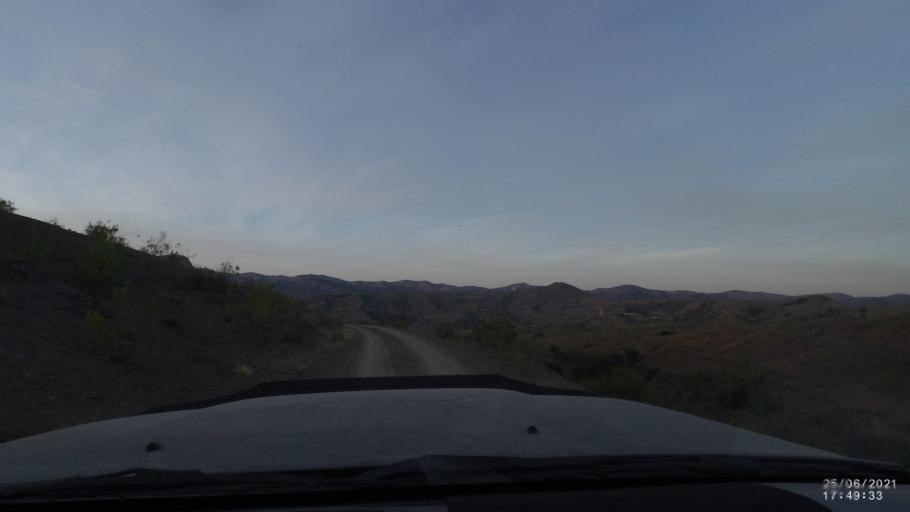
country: BO
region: Cochabamba
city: Mizque
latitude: -17.9556
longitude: -65.6423
